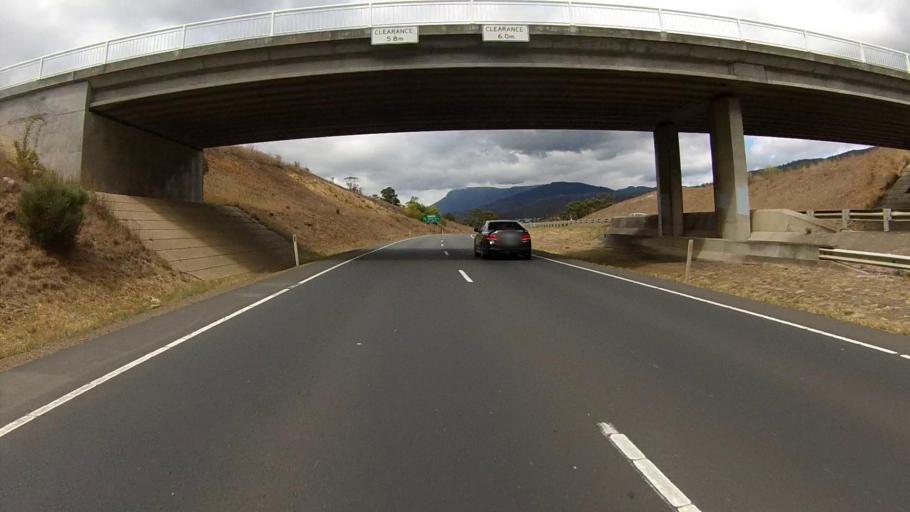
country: AU
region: Tasmania
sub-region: Glenorchy
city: Austins Ferry
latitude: -42.7734
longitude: 147.2391
